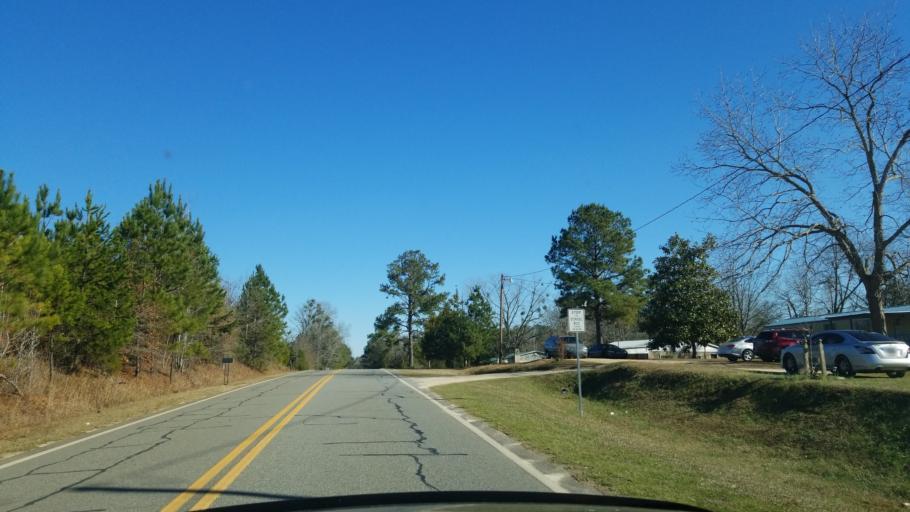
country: US
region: Georgia
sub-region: Talbot County
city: Talbotton
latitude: 32.6727
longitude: -84.5272
